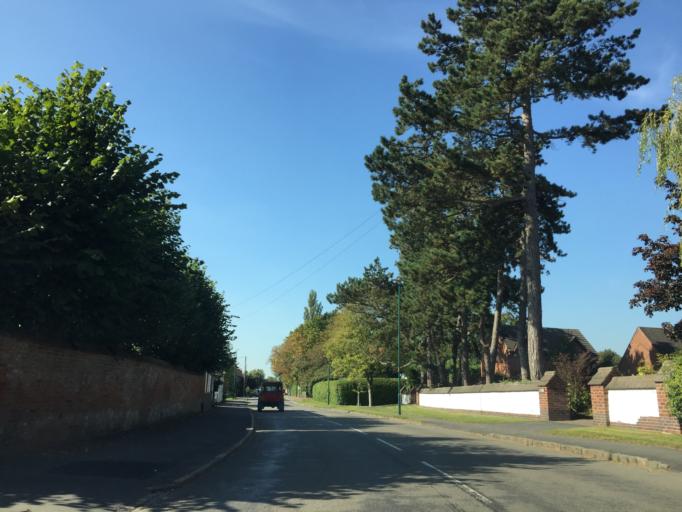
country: GB
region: England
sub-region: Leicestershire
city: Queniborough
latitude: 52.7042
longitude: -1.0443
